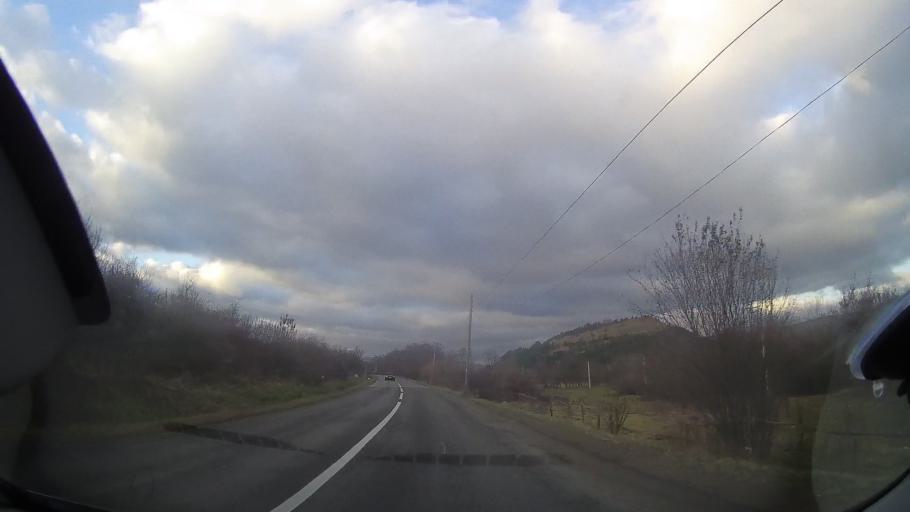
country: RO
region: Cluj
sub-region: Comuna Calatele
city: Calatele
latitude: 46.7828
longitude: 23.0049
